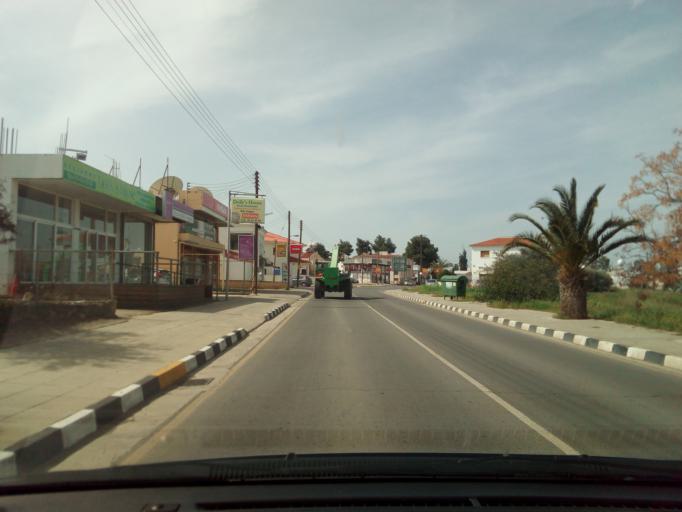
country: CY
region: Lefkosia
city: Kato Deftera
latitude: 35.0845
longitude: 33.2746
